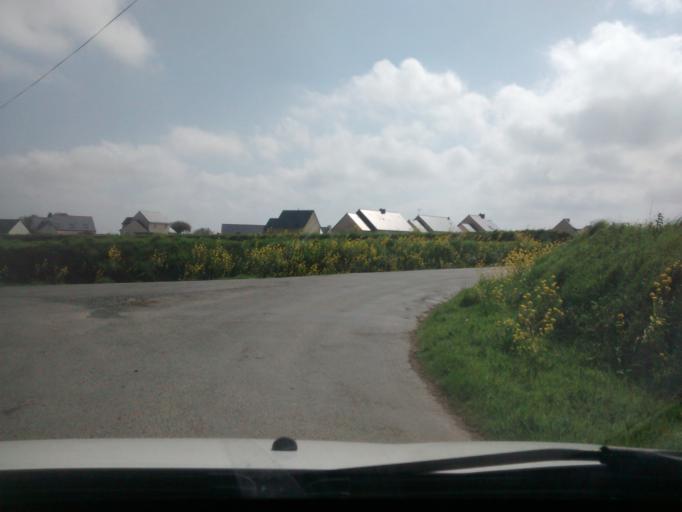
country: FR
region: Brittany
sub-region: Departement des Cotes-d'Armor
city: Penvenan
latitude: 48.8103
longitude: -3.3040
